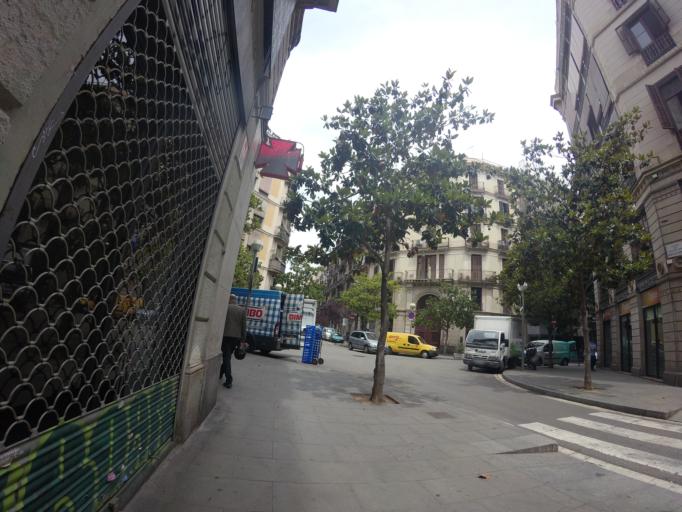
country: ES
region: Catalonia
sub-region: Provincia de Barcelona
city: Ciutat Vella
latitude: 41.3819
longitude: 2.1694
